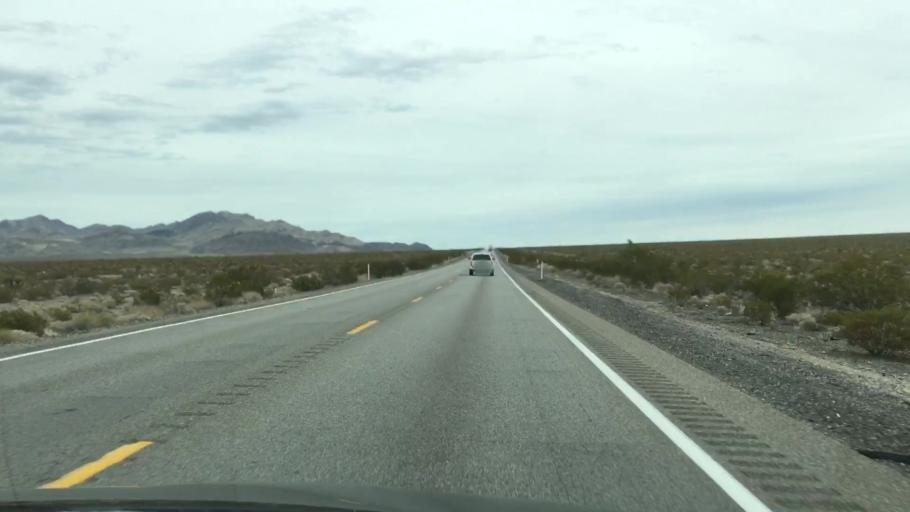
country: US
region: Nevada
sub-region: Nye County
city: Pahrump
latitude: 36.5913
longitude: -116.0348
